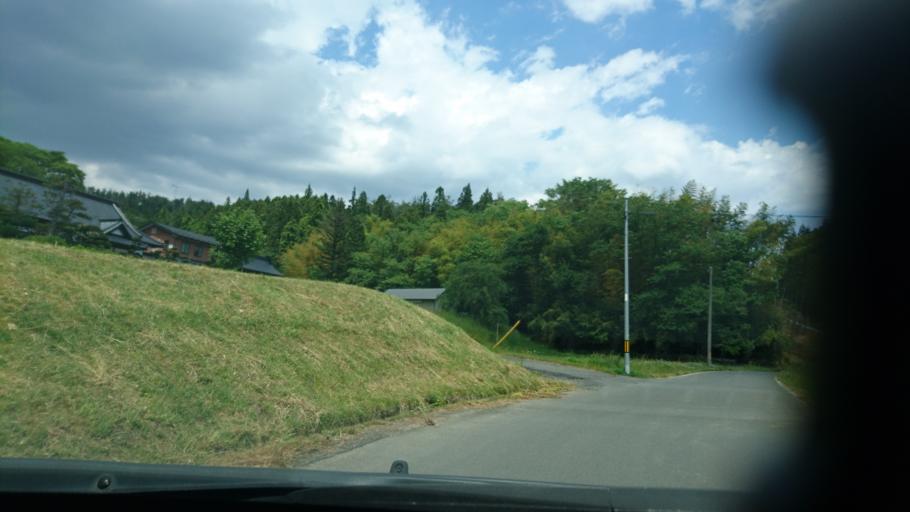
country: JP
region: Iwate
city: Ichinoseki
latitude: 38.9783
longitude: 141.0911
